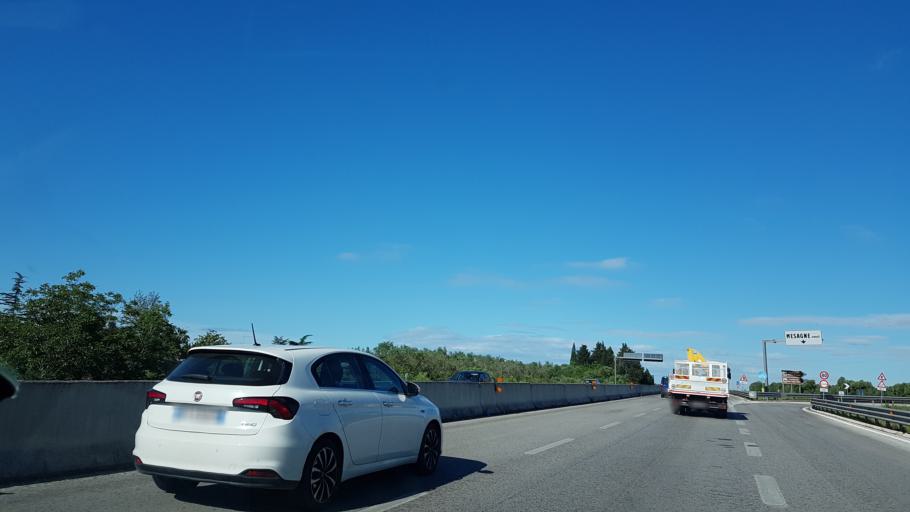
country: IT
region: Apulia
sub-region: Provincia di Brindisi
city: Mesagne
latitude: 40.5675
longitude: 17.7845
